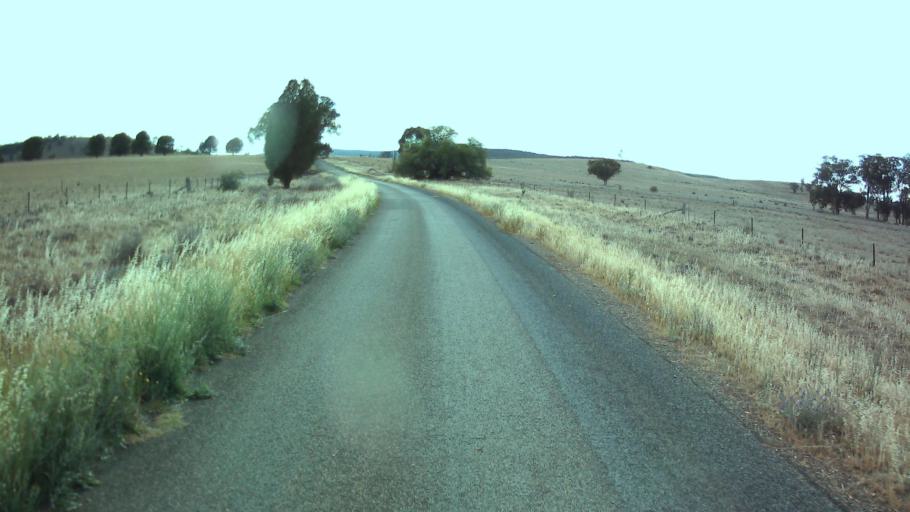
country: AU
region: New South Wales
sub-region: Weddin
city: Grenfell
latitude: -33.8457
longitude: 148.2483
